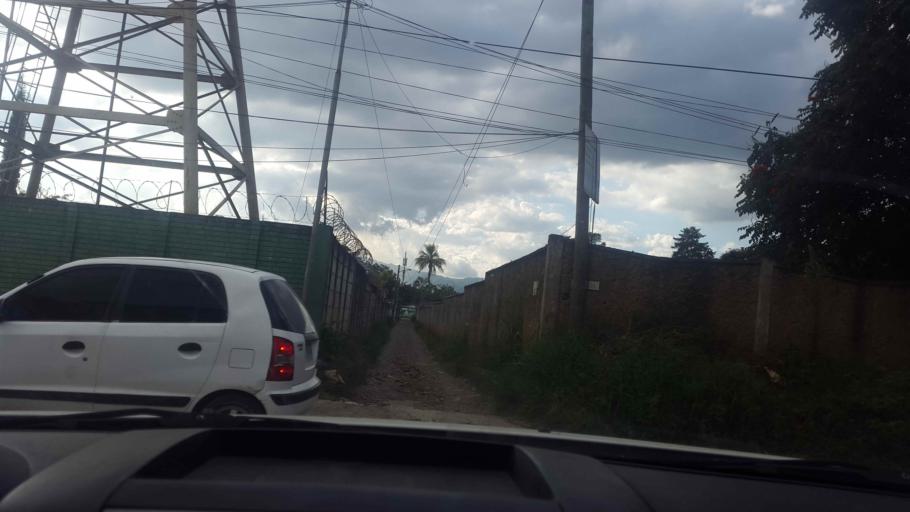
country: GT
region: Guatemala
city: Petapa
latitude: 14.5168
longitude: -90.5369
